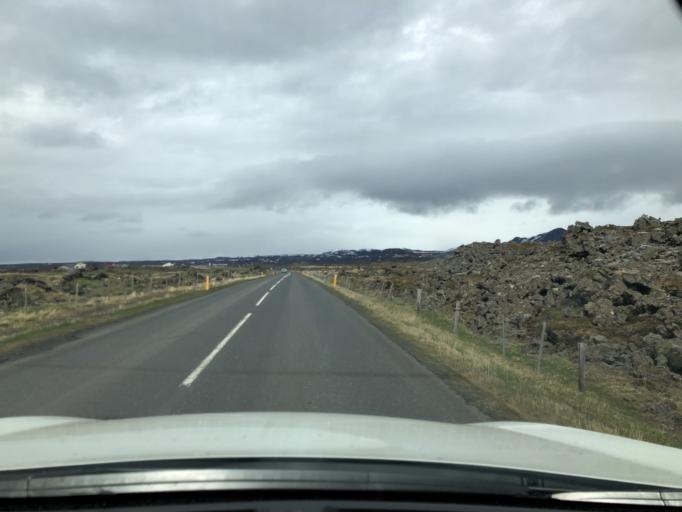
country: IS
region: Northeast
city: Laugar
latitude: 65.6147
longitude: -16.9157
